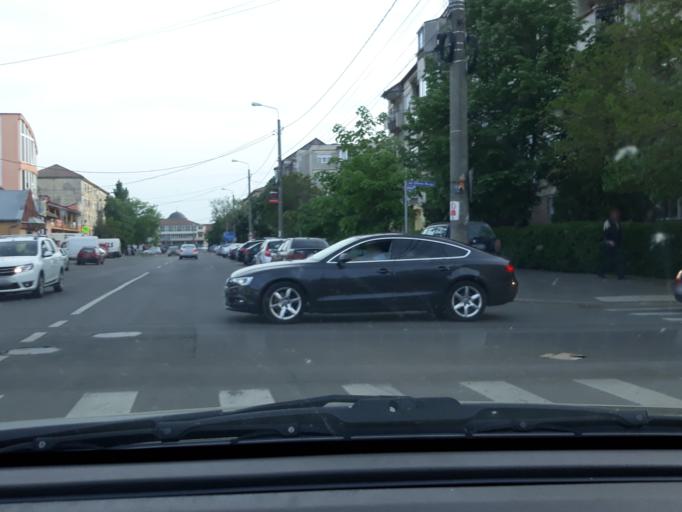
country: RO
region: Bihor
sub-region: Comuna Biharea
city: Oradea
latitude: 47.0462
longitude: 21.9565
